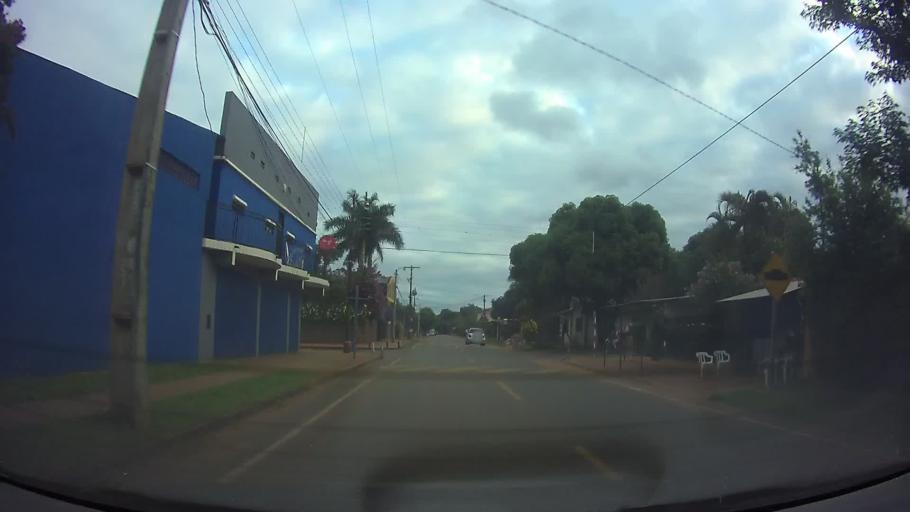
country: PY
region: Central
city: San Lorenzo
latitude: -25.2842
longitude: -57.4866
